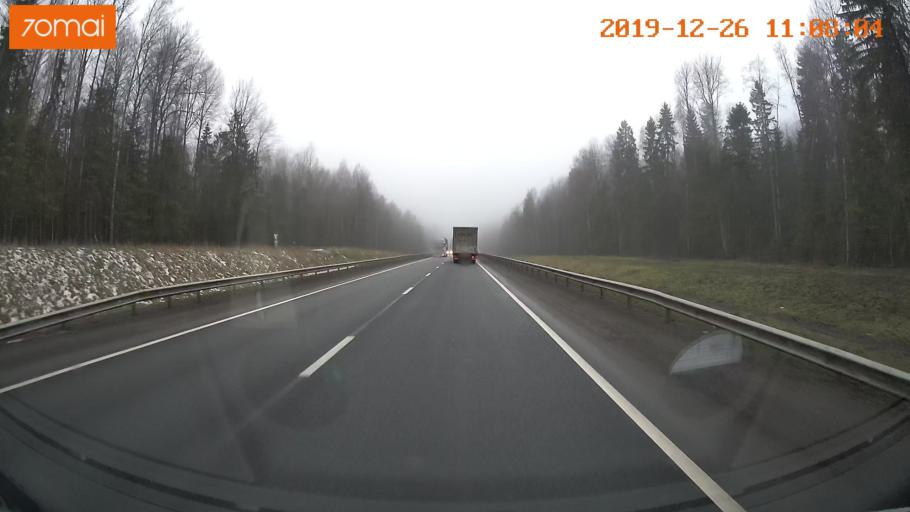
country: RU
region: Vologda
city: Molochnoye
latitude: 59.1372
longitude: 39.2820
